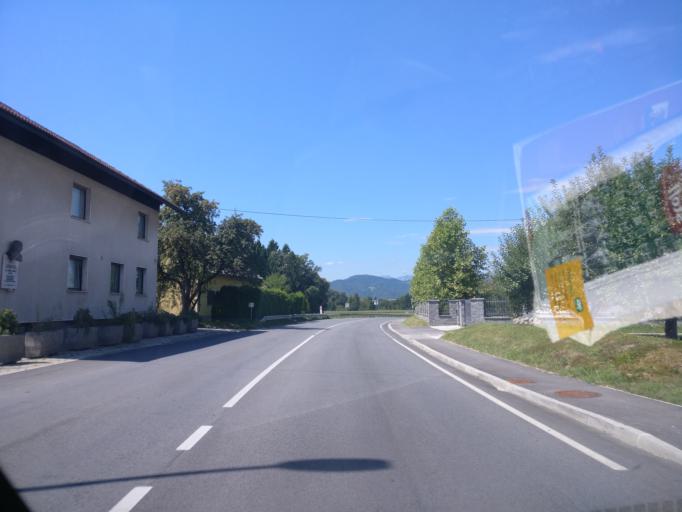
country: SI
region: Skofja Loka
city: Sv. Duh
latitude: 46.1669
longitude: 14.3512
